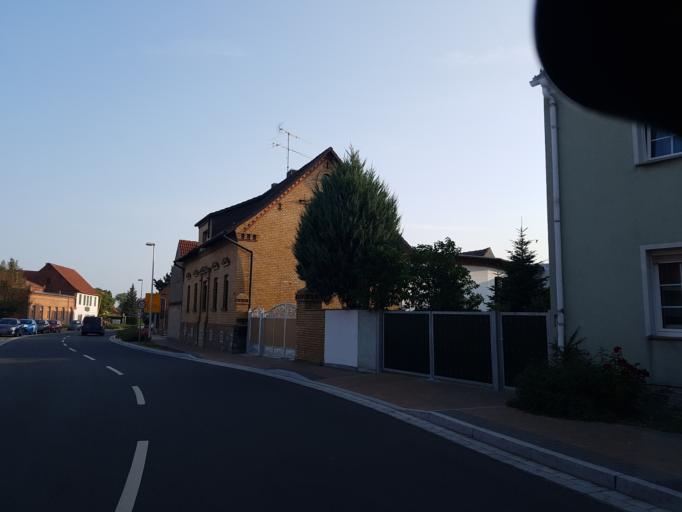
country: DE
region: Saxony-Anhalt
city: Pretzsch
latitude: 51.7540
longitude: 12.7515
